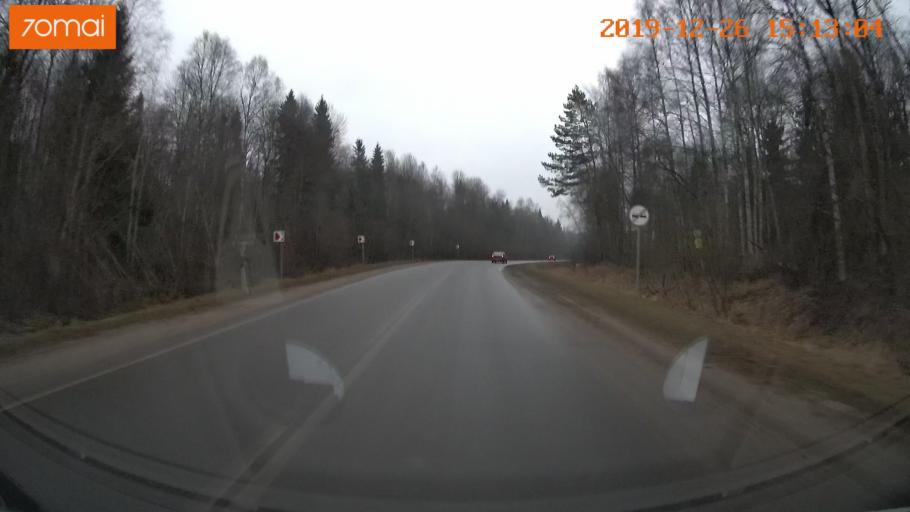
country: RU
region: Jaroslavl
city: Rybinsk
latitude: 58.1213
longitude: 38.8827
